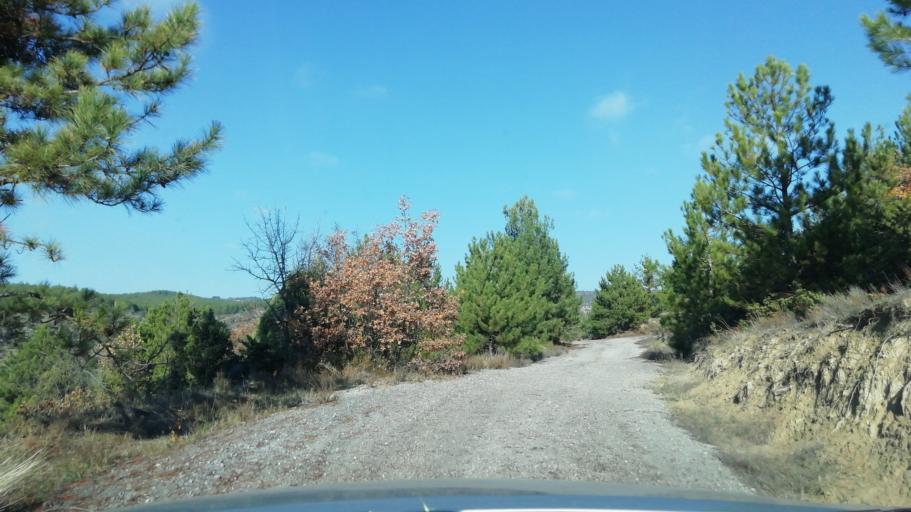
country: TR
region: Karabuk
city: Safranbolu
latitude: 41.2350
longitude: 32.7825
